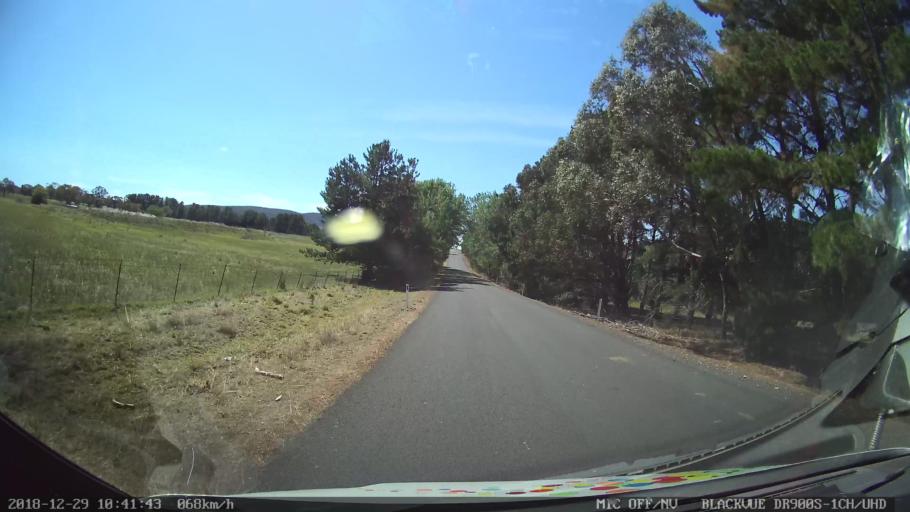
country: AU
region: New South Wales
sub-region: Palerang
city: Bungendore
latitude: -35.0280
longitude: 149.5225
